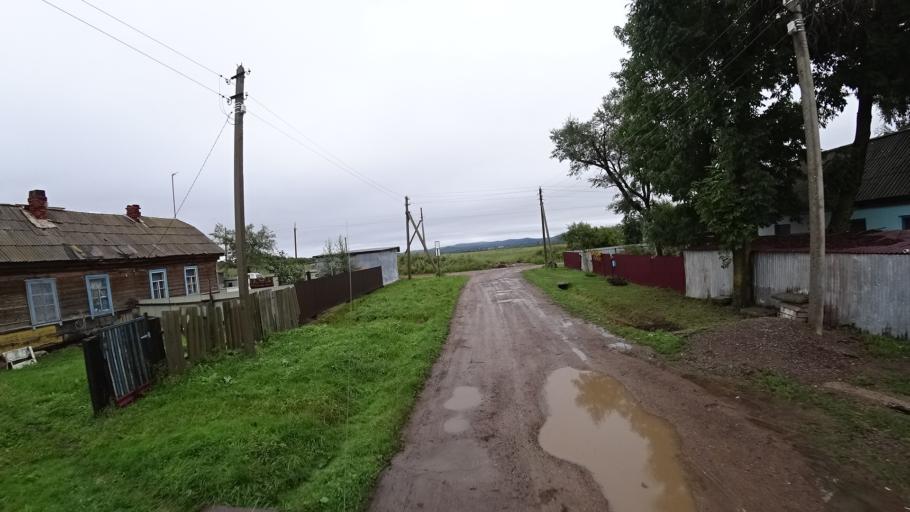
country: RU
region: Primorskiy
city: Monastyrishche
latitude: 44.2344
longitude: 132.4646
